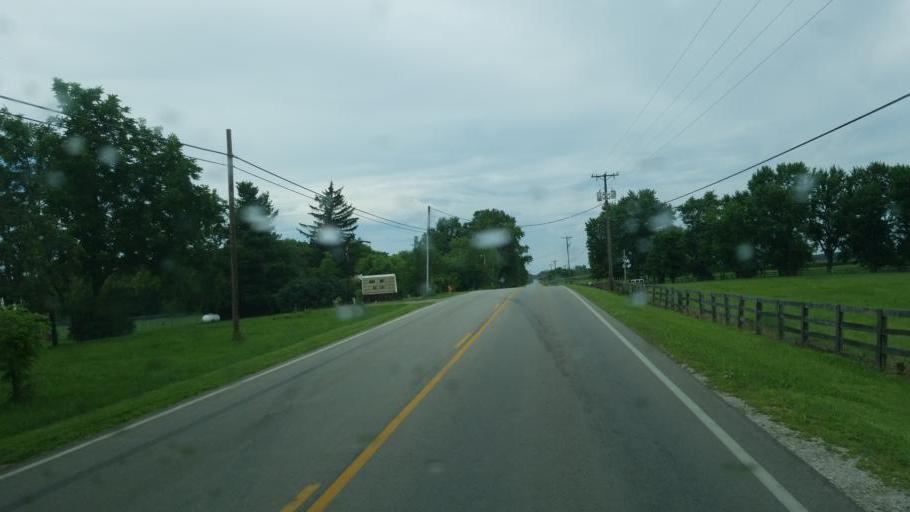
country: US
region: Ohio
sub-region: Pickaway County
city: Circleville
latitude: 39.6475
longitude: -82.9525
